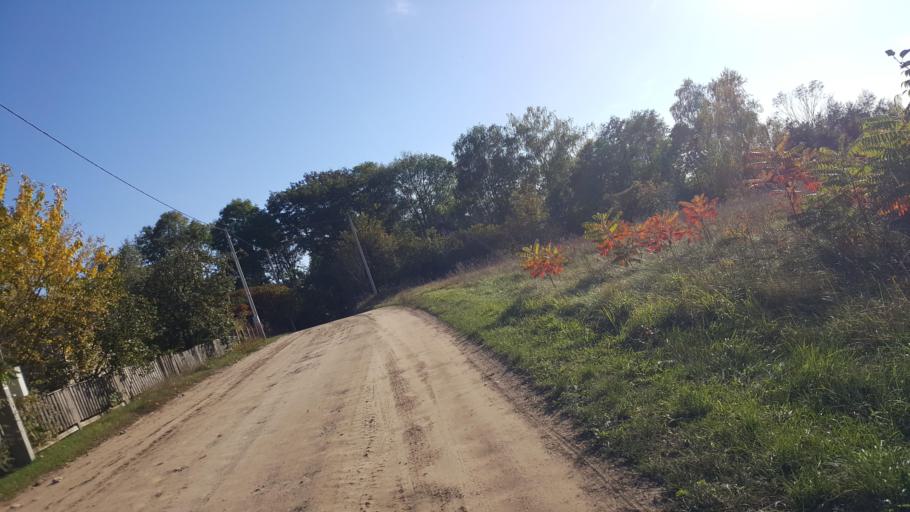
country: BY
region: Brest
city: Kamyanyets
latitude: 52.3937
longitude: 23.8849
